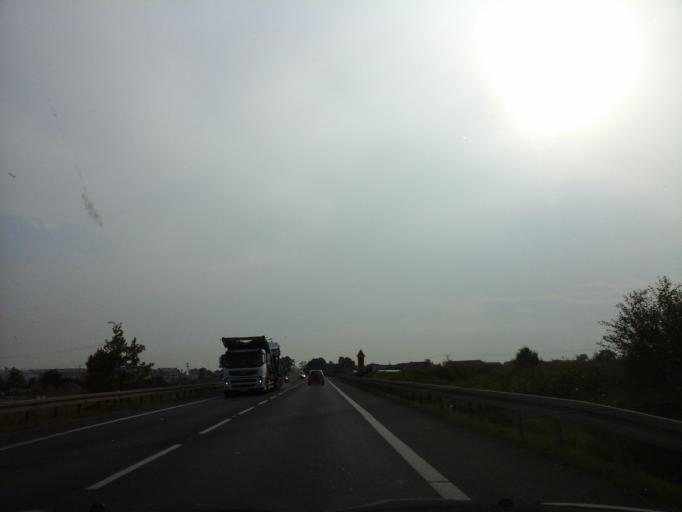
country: PL
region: Greater Poland Voivodeship
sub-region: Powiat koscianski
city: Koscian
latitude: 52.0948
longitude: 16.6295
